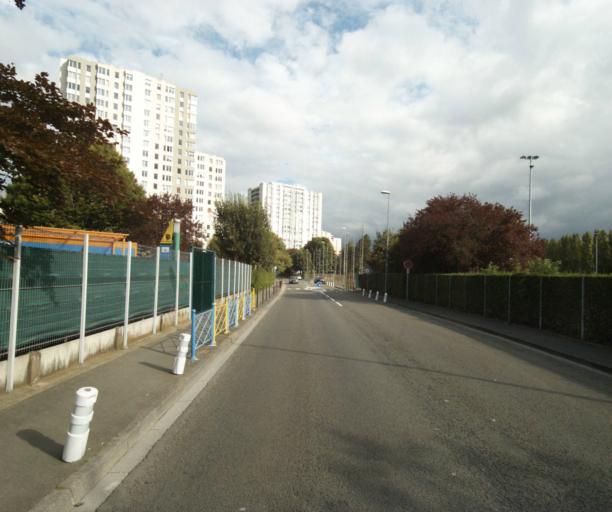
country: FR
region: Nord-Pas-de-Calais
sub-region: Departement du Nord
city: La Madeleine
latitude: 50.6517
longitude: 3.0650
